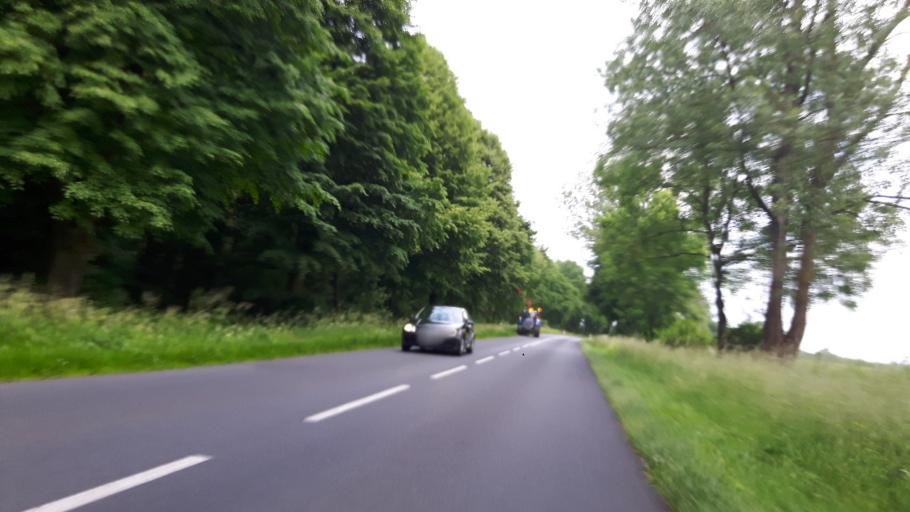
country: PL
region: West Pomeranian Voivodeship
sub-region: Powiat gryficki
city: Trzebiatow
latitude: 53.9966
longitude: 15.2392
